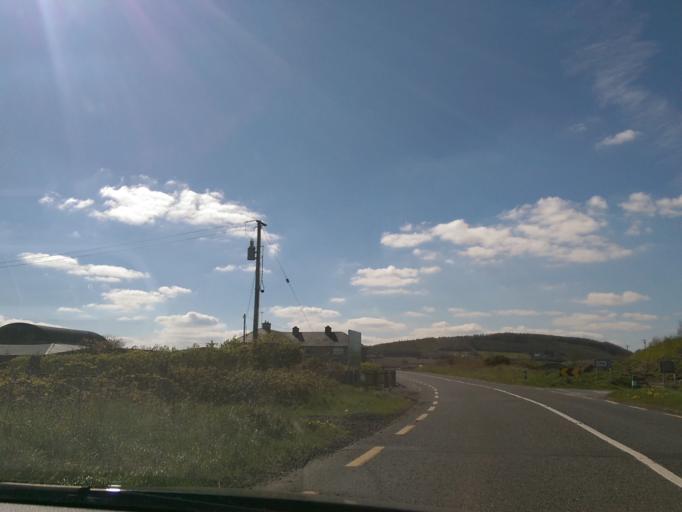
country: IE
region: Leinster
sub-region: Laois
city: Stradbally
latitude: 53.0221
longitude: -7.1761
